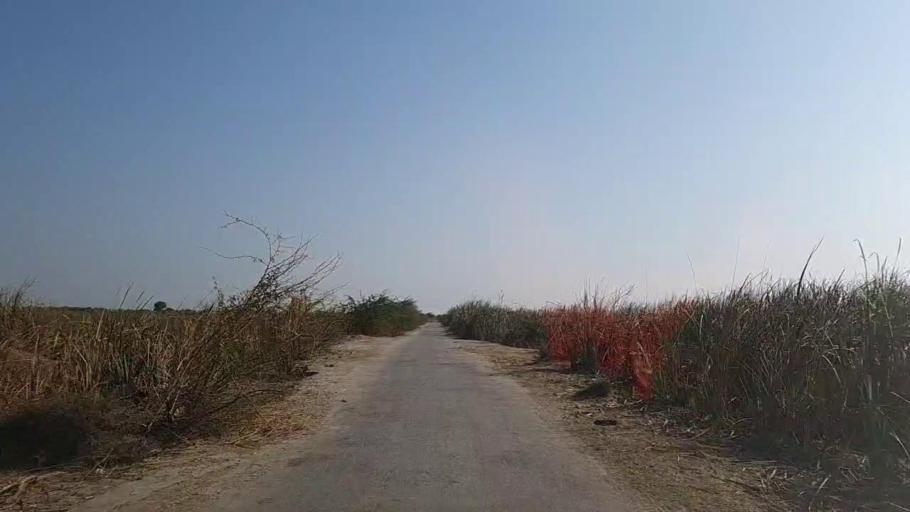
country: PK
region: Sindh
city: Sanghar
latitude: 25.9386
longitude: 69.0562
